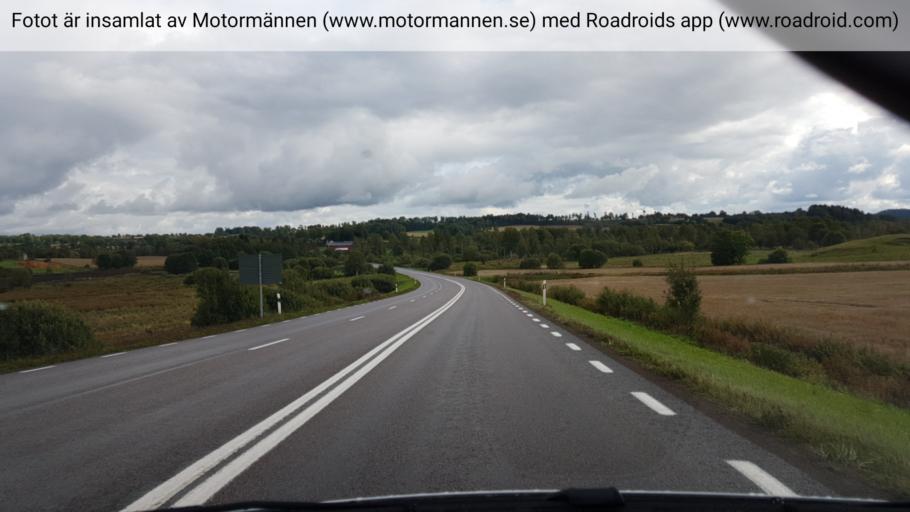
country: SE
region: Vaestra Goetaland
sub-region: Falkopings Kommun
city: Akarp
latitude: 58.1367
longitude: 13.6423
